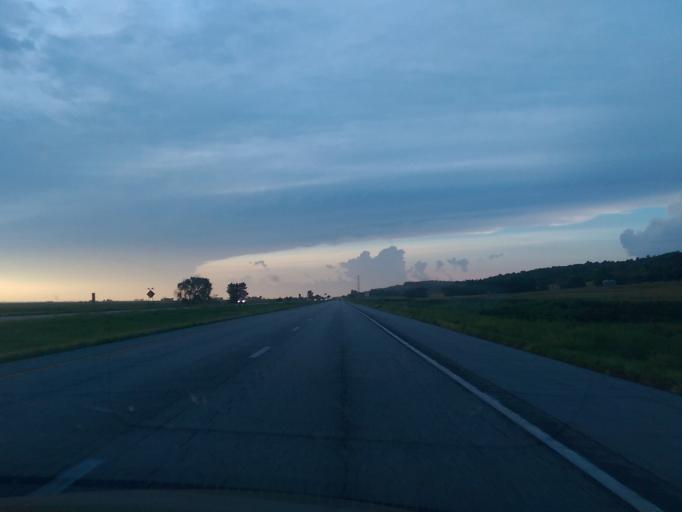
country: US
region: Missouri
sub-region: Atchison County
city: Rock Port
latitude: 40.3748
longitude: -95.5374
